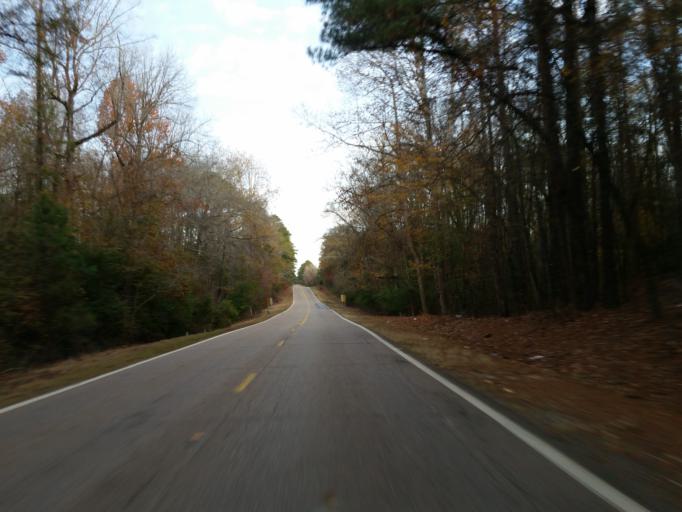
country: US
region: Alabama
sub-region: Sumter County
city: York
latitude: 32.4239
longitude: -88.4247
